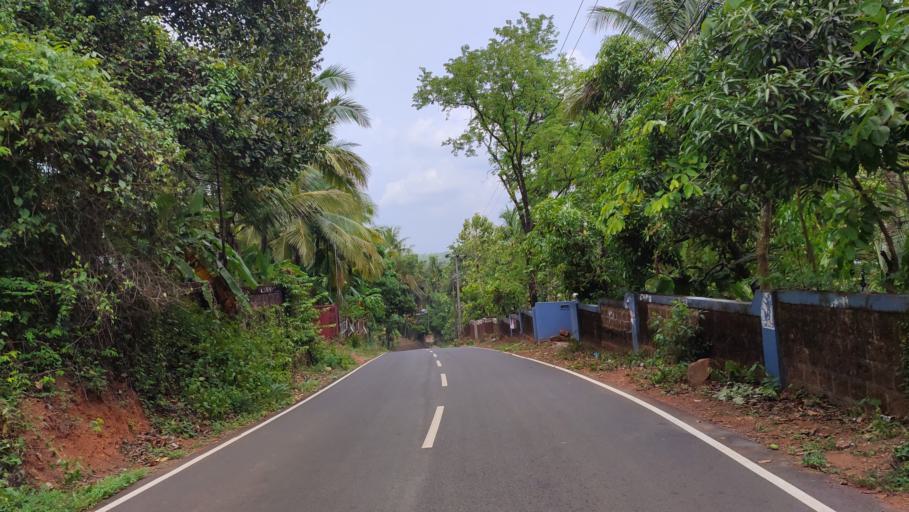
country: IN
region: Kerala
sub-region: Kasaragod District
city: Kannangad
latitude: 12.3207
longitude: 75.1095
